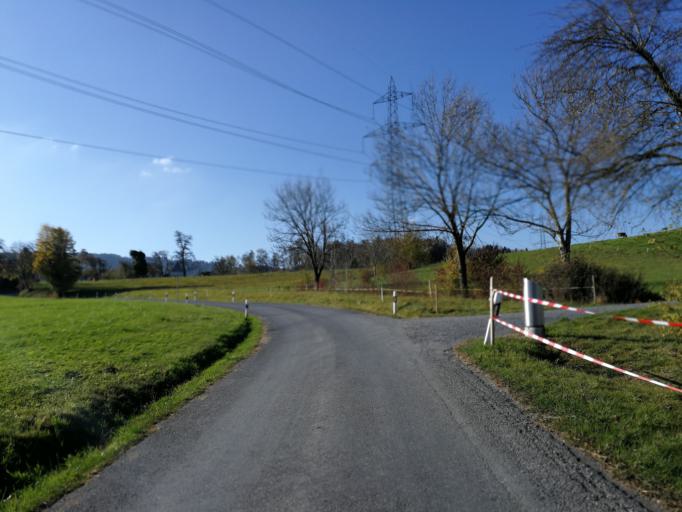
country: CH
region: Zurich
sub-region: Bezirk Uster
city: Egg
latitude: 47.3031
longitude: 8.7026
